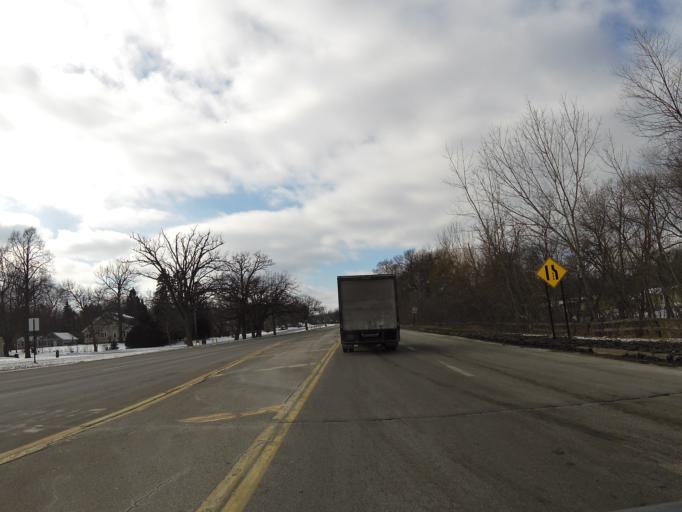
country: US
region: Minnesota
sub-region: Hennepin County
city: Minnetonka Mills
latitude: 44.9209
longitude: -93.4279
